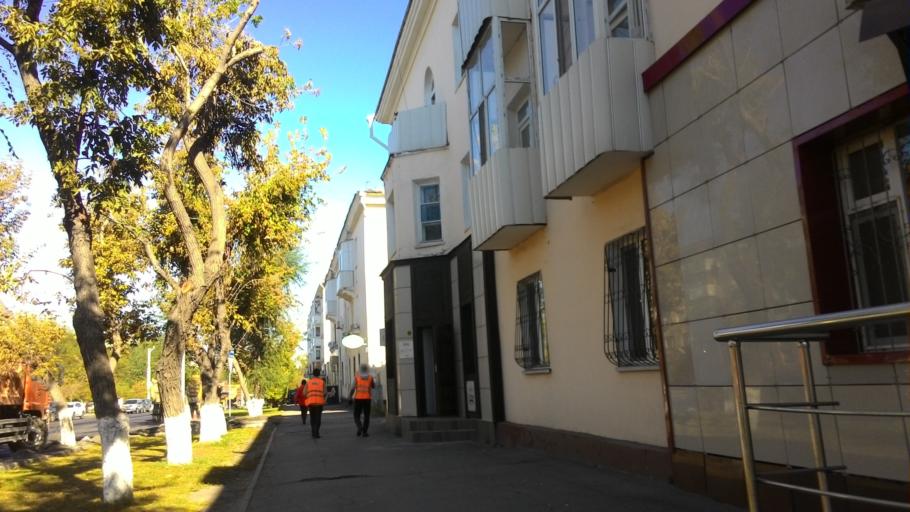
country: KZ
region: Astana Qalasy
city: Astana
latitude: 51.1688
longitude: 71.4158
